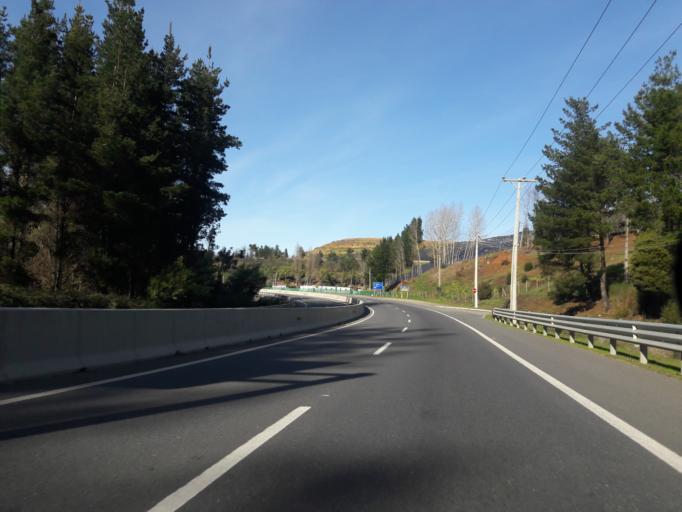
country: CL
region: Biobio
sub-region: Provincia de Concepcion
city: Chiguayante
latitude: -36.8620
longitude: -72.8582
